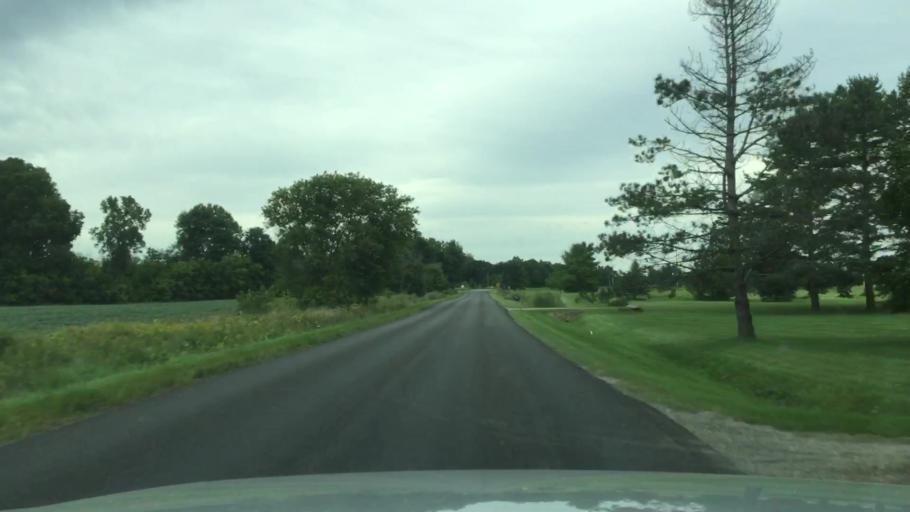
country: US
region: Michigan
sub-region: Shiawassee County
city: Durand
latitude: 42.8651
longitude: -84.0471
